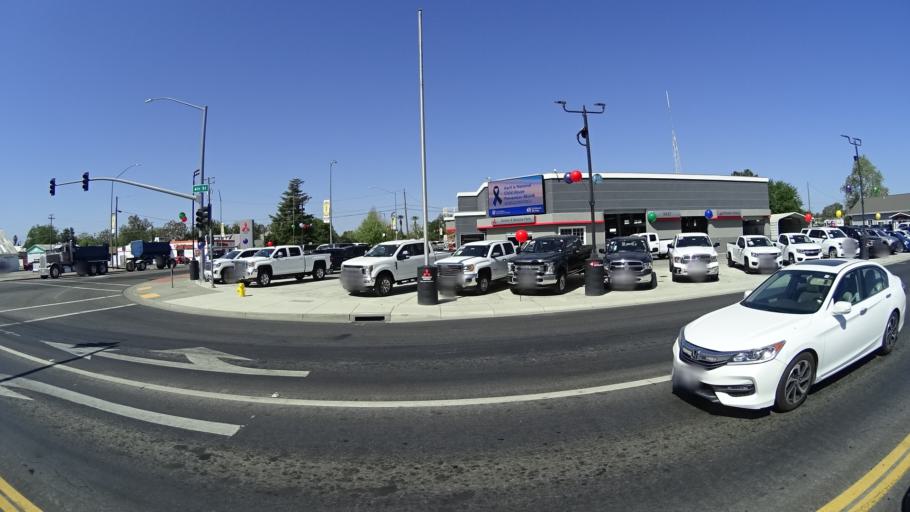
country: US
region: California
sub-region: Glenn County
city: Orland
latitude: 39.7476
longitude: -122.1975
